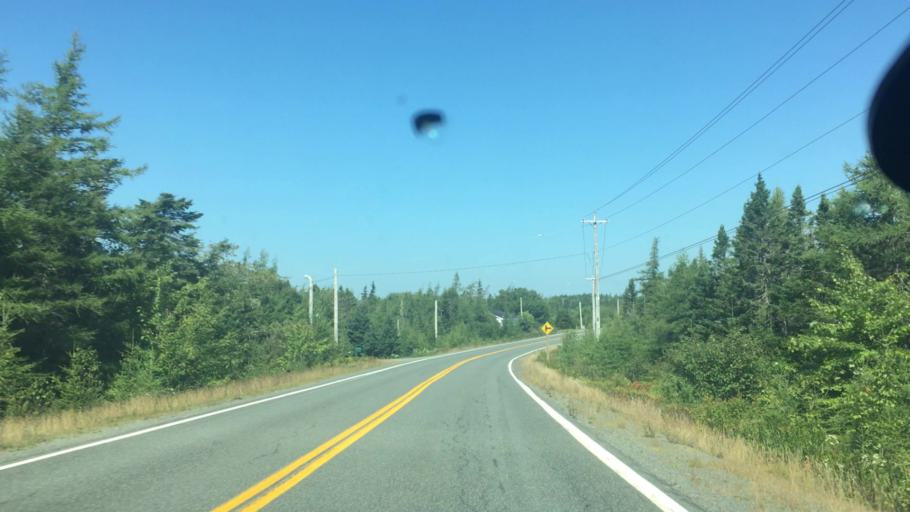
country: CA
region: Nova Scotia
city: Antigonish
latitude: 44.9965
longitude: -62.0993
